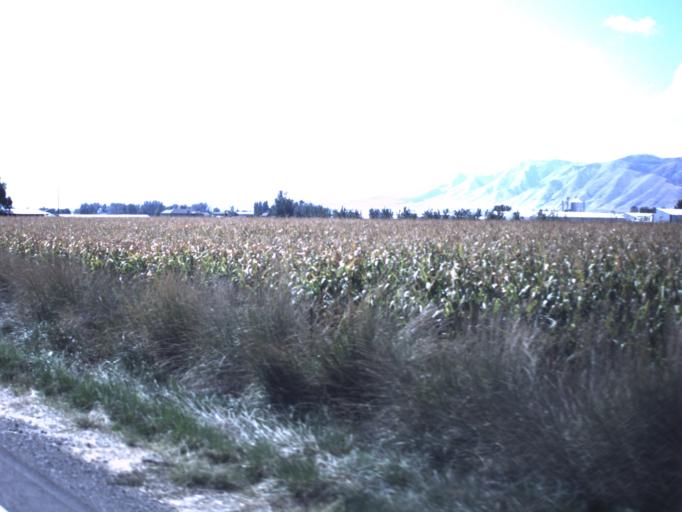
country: US
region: Utah
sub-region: Utah County
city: Benjamin
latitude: 40.1201
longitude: -111.7305
